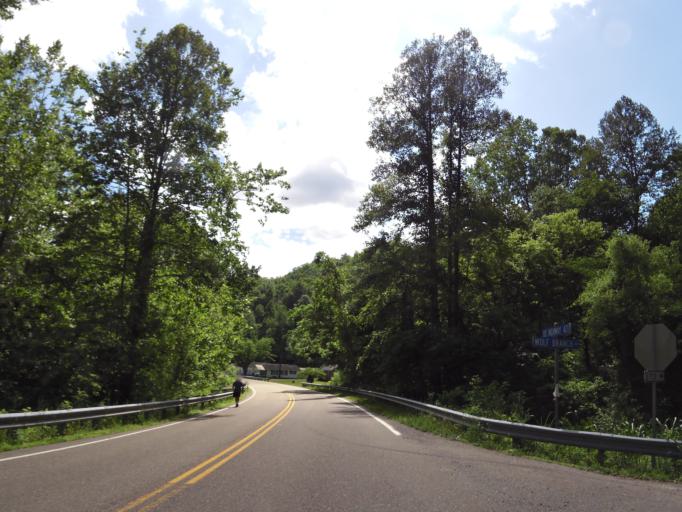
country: US
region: Virginia
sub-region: Lee County
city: Pennington Gap
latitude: 36.7686
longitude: -83.0747
